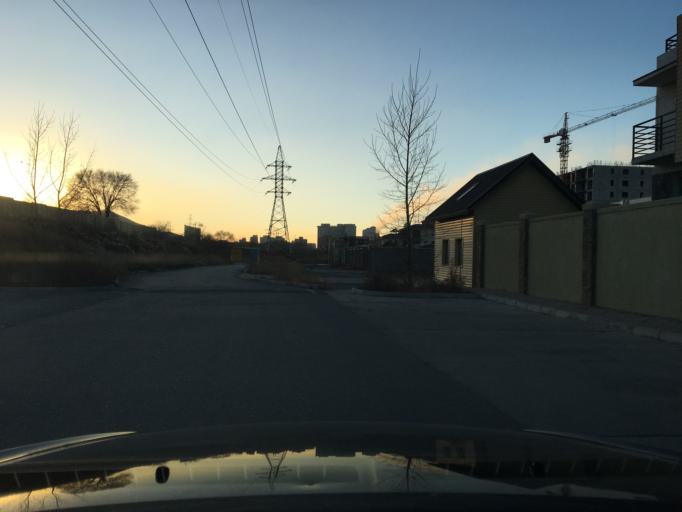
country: MN
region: Ulaanbaatar
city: Ulaanbaatar
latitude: 47.8928
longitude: 106.9196
